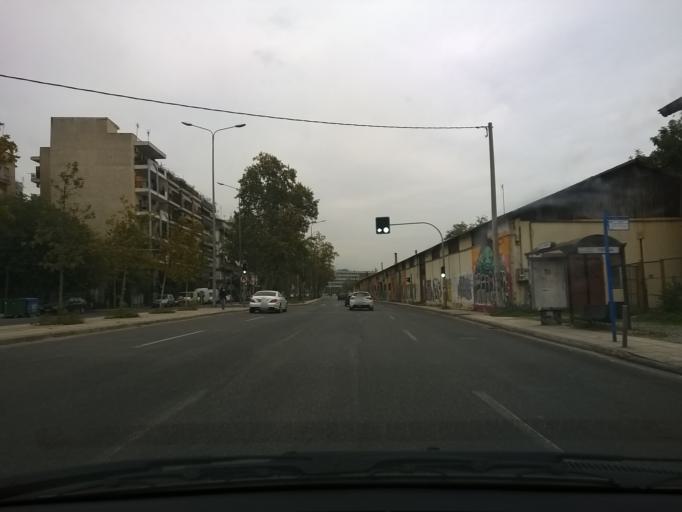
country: GR
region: Central Macedonia
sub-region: Nomos Thessalonikis
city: Thessaloniki
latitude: 40.6412
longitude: 22.9269
